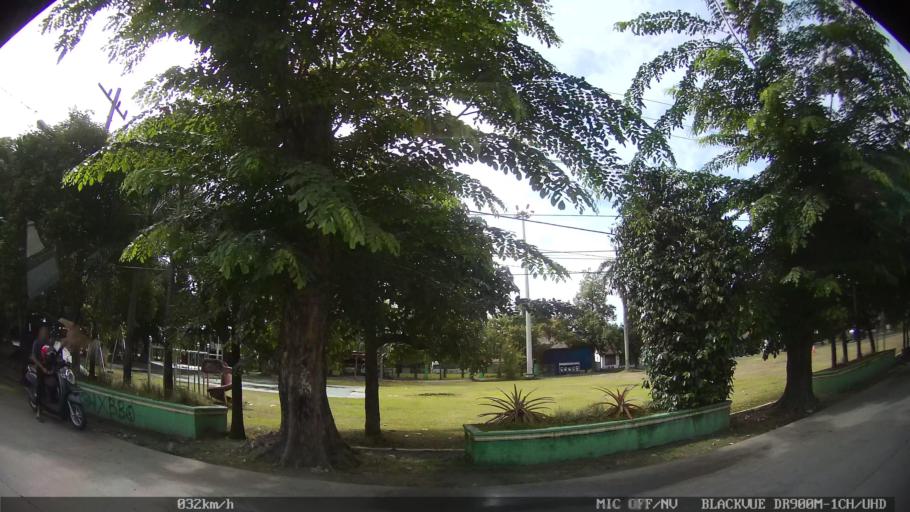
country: ID
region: North Sumatra
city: Medan
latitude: 3.6229
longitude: 98.6712
